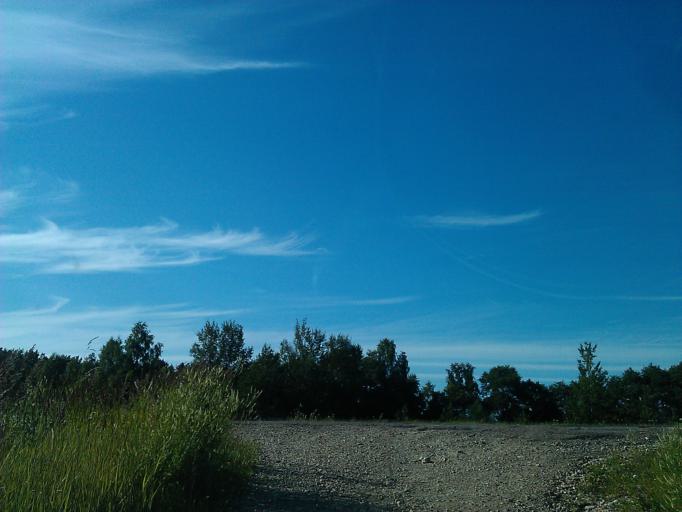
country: LV
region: Incukalns
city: Incukalns
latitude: 57.1283
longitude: 24.7171
